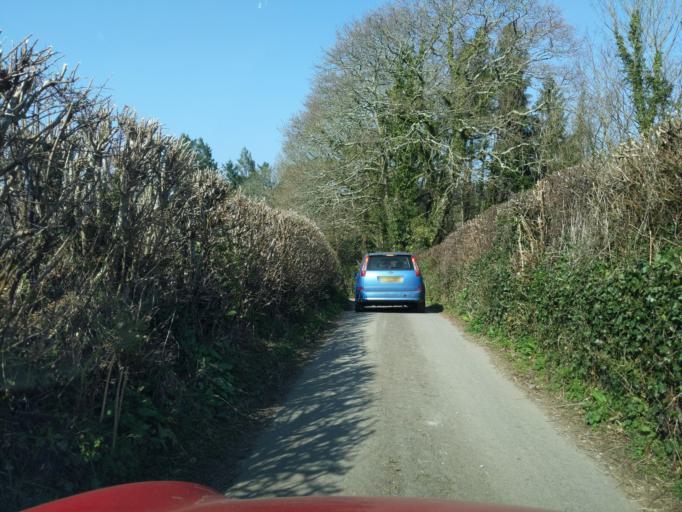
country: GB
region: England
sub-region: Devon
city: Bere Alston
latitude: 50.4535
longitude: -4.1514
